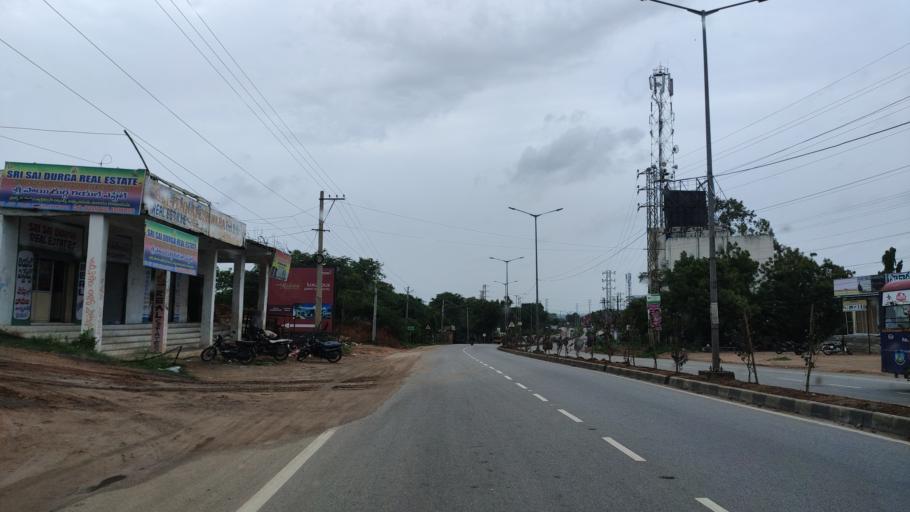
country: IN
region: Telangana
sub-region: Rangareddi
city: Secunderabad
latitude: 17.5942
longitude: 78.5694
